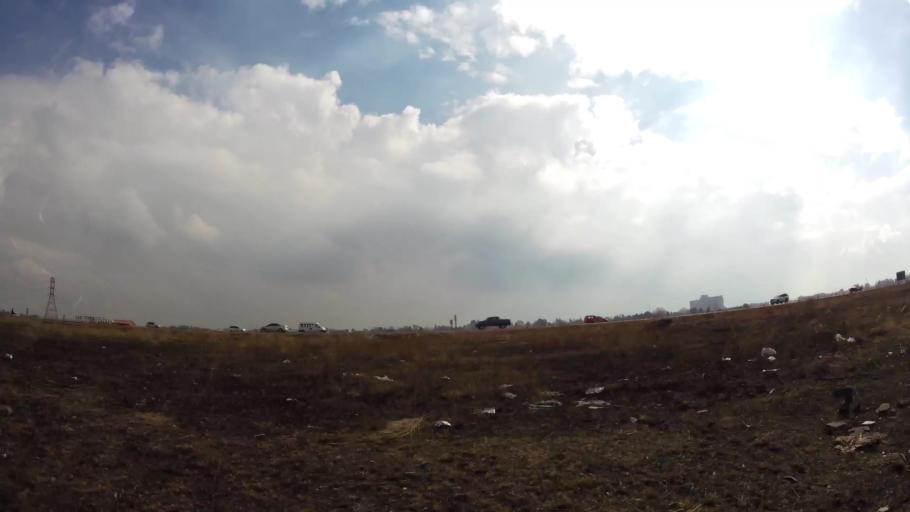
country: ZA
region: Gauteng
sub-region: Sedibeng District Municipality
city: Vereeniging
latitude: -26.6652
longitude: 27.9123
